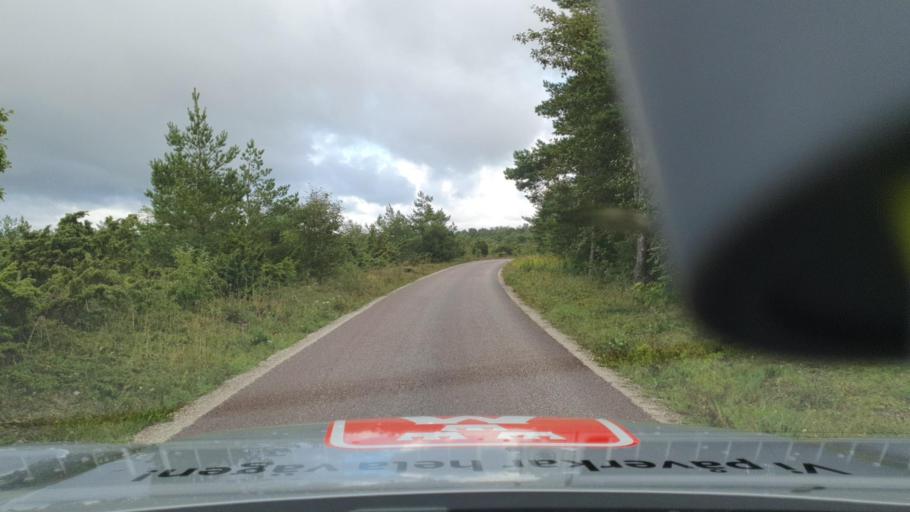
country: SE
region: Gotland
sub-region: Gotland
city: Hemse
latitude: 56.9800
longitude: 18.1957
